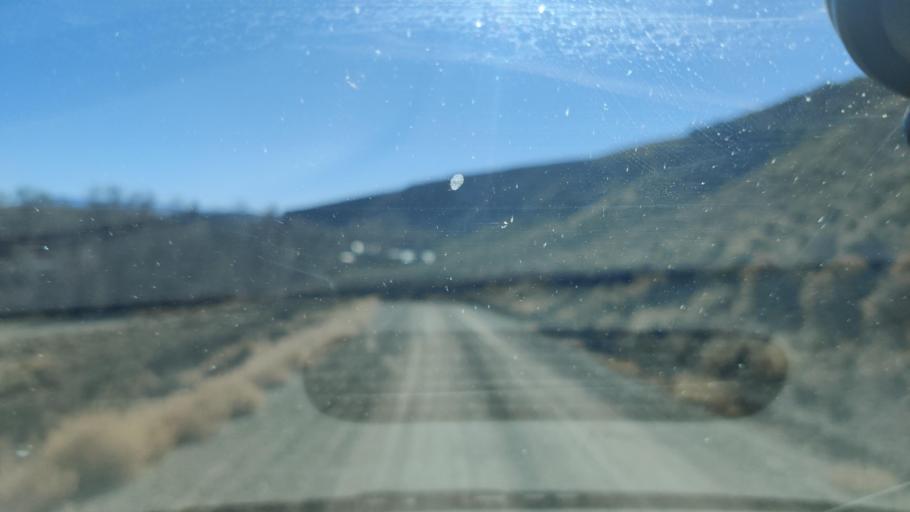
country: US
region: Colorado
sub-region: Gunnison County
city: Gunnison
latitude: 38.5417
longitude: -106.9518
